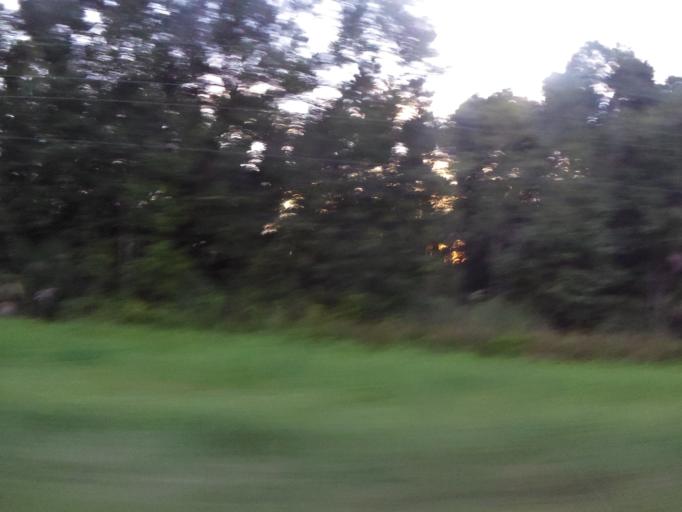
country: US
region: Georgia
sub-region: Camden County
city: Kingsland
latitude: 30.8390
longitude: -81.6981
